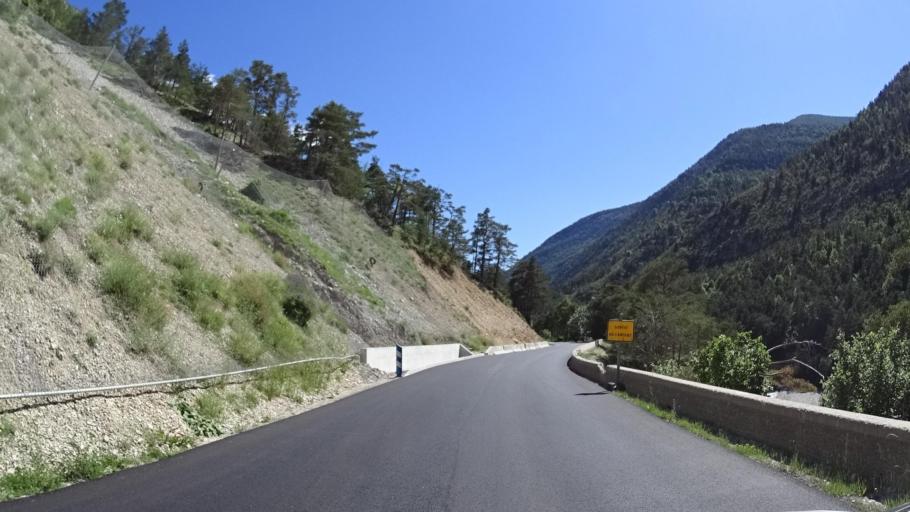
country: FR
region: Provence-Alpes-Cote d'Azur
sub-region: Departement des Alpes-de-Haute-Provence
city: Annot
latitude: 44.0595
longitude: 6.5759
